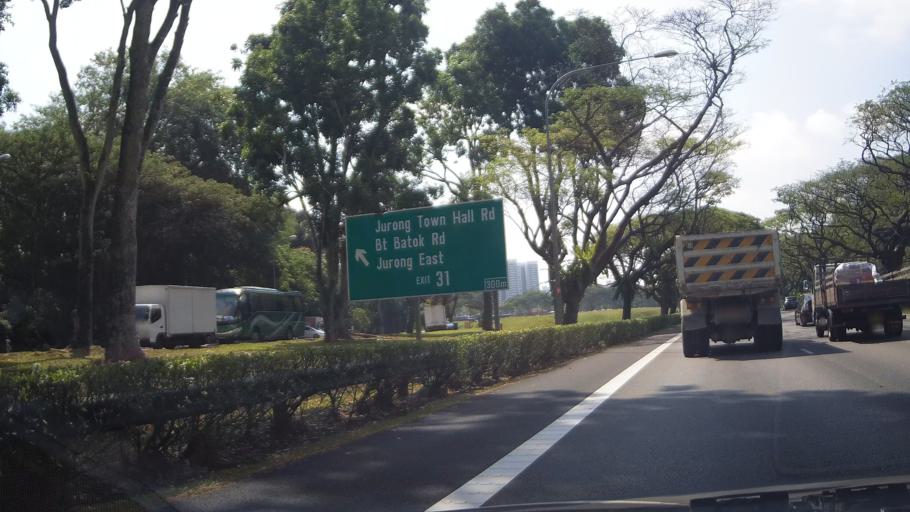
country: MY
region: Johor
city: Johor Bahru
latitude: 1.3507
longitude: 103.7327
